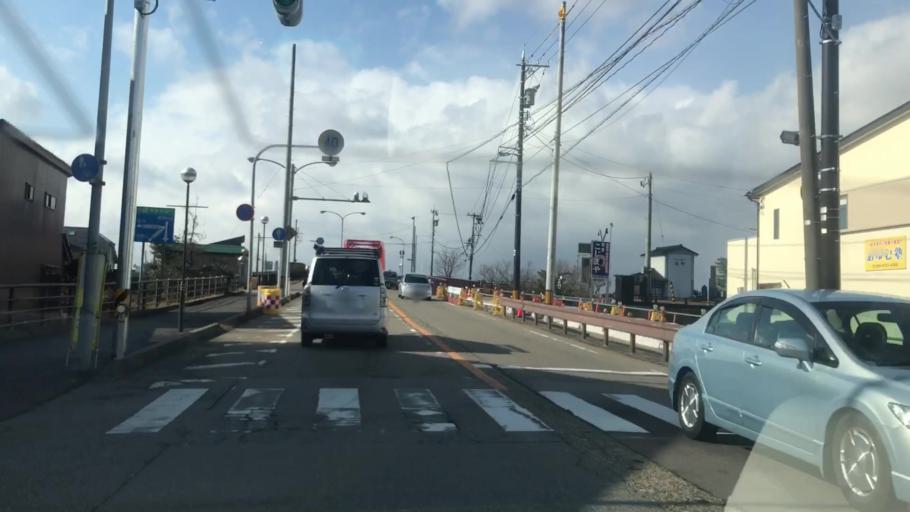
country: JP
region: Toyama
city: Takaoka
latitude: 36.7342
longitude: 137.0469
